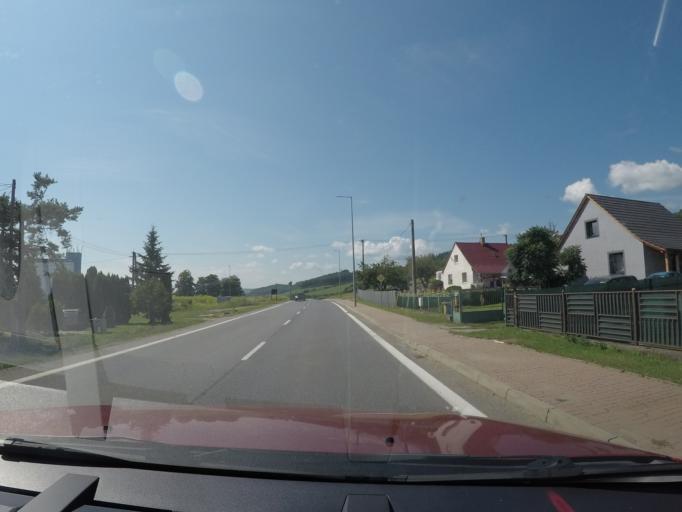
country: SK
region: Presovsky
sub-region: Okres Presov
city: Presov
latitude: 48.9220
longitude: 21.2411
